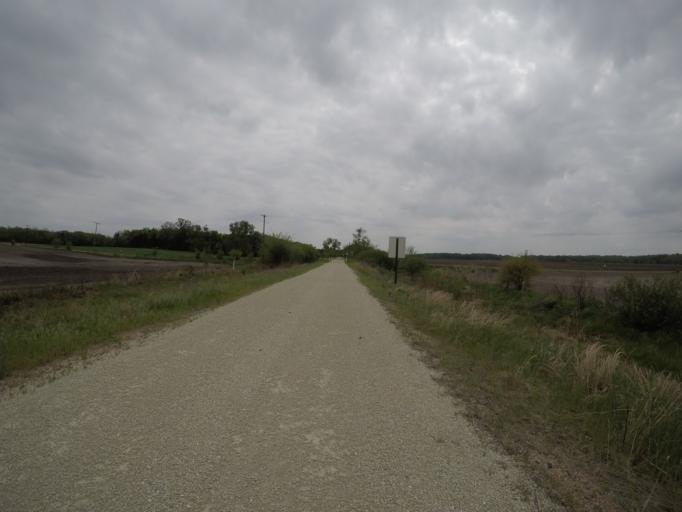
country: US
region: Nebraska
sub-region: Gage County
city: Wymore
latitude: 40.0599
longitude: -96.5793
